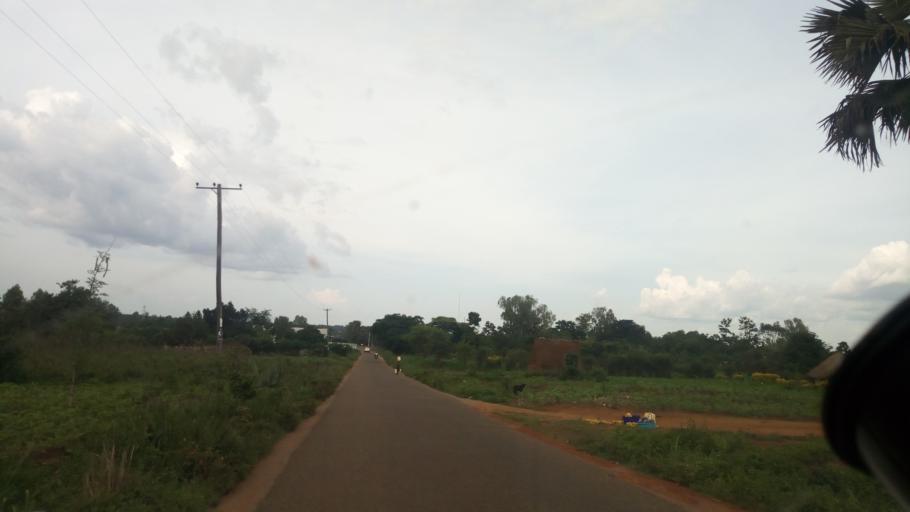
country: UG
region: Northern Region
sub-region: Lira District
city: Lira
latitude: 2.2582
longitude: 32.8530
